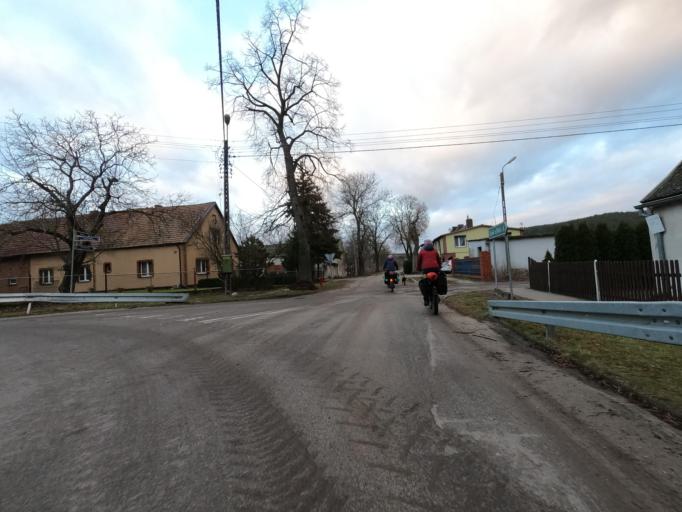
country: PL
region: Greater Poland Voivodeship
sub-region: Powiat pilski
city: Bialosliwie
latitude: 53.1122
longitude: 17.2005
